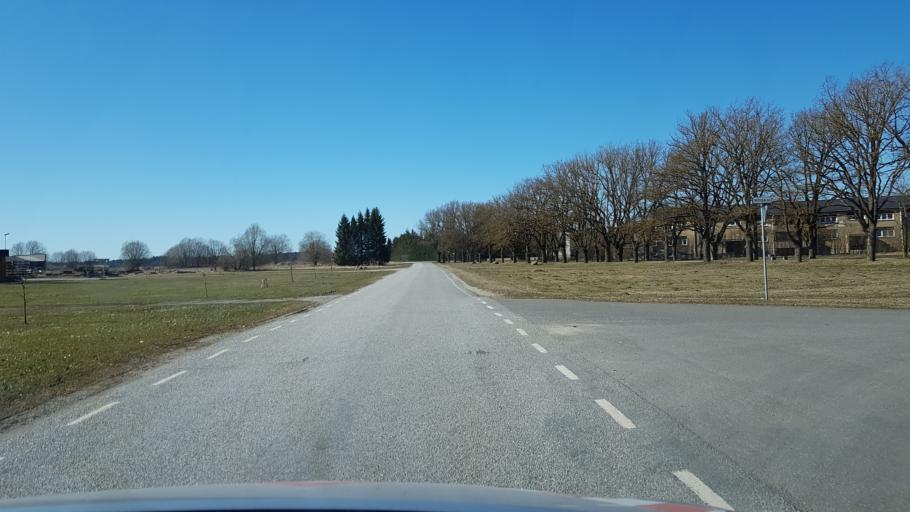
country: EE
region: Laeaene-Virumaa
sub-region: Viru-Nigula vald
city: Kunda
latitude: 59.3939
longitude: 26.5648
